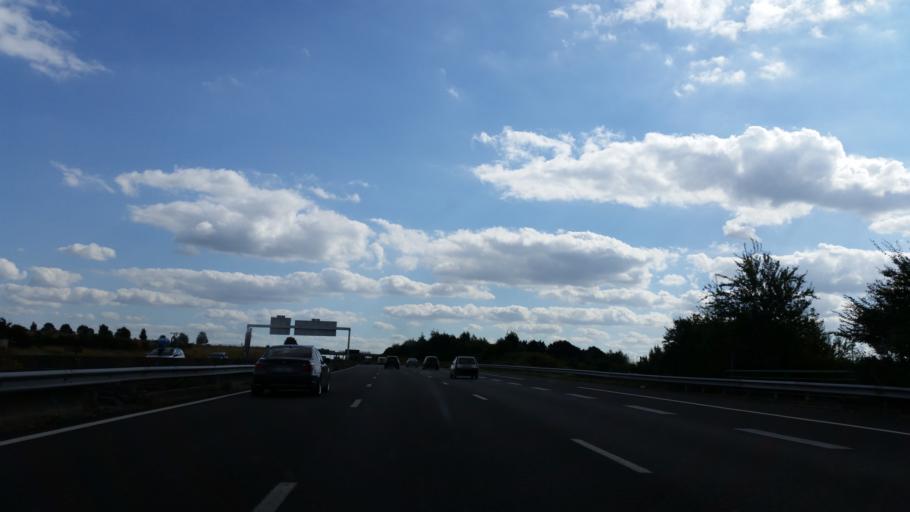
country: FR
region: Picardie
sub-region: Departement de la Somme
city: Moislains
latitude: 50.0111
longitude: 2.8779
